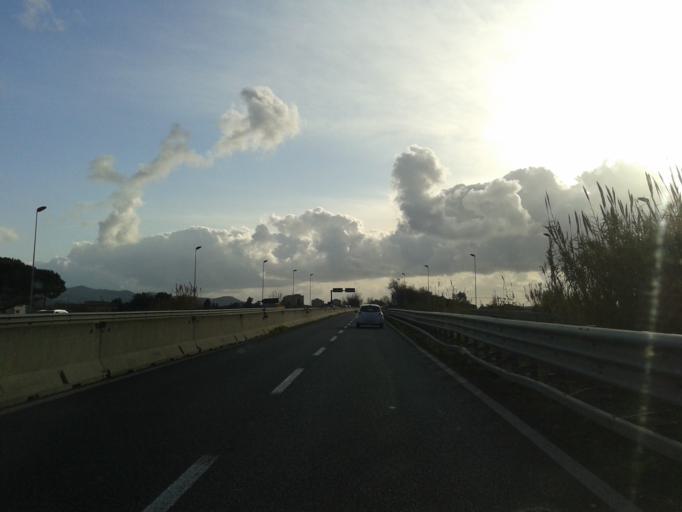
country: IT
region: Tuscany
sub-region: Provincia di Livorno
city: Livorno
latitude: 43.5490
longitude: 10.3421
